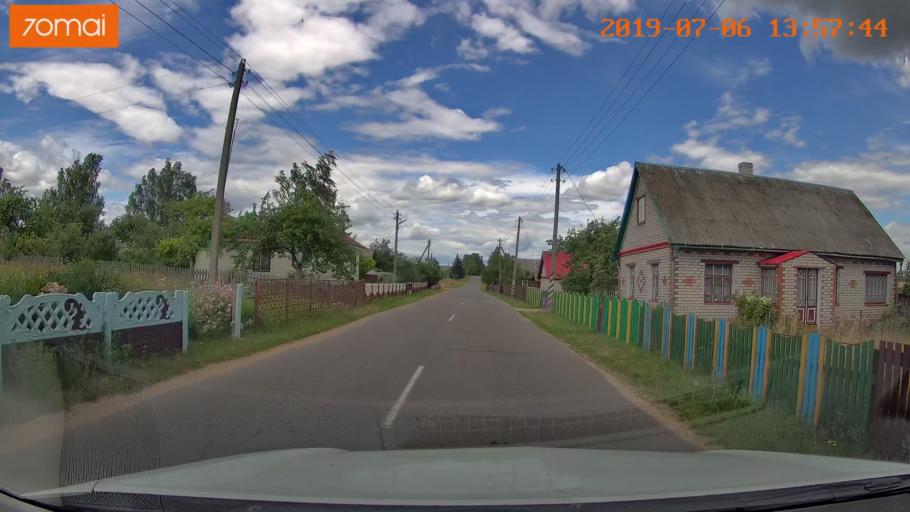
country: BY
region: Minsk
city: Ivyanyets
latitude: 53.7768
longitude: 26.8070
